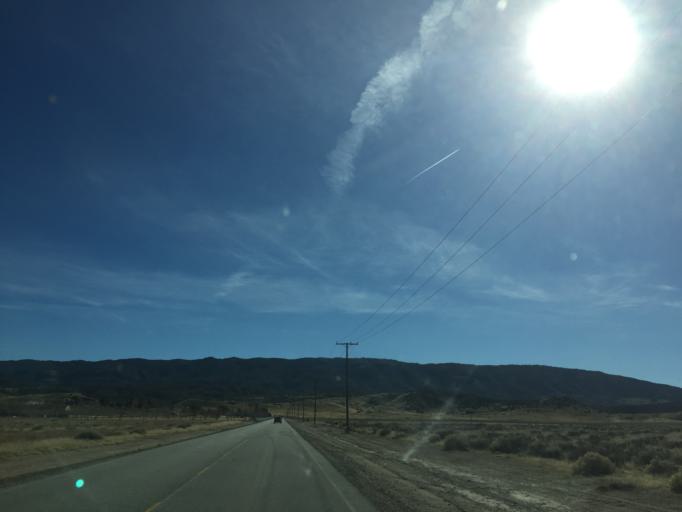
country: US
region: California
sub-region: Kern County
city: Lebec
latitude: 34.7915
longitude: -118.6611
